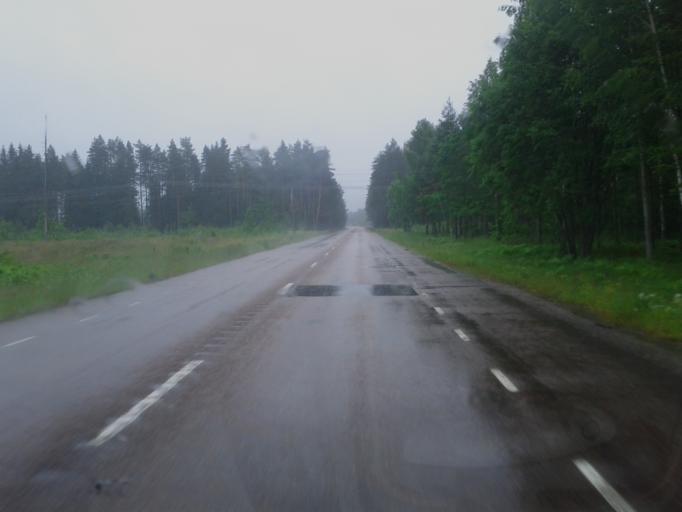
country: SE
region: Uppsala
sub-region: Alvkarleby Kommun
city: AElvkarleby
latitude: 60.5558
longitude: 17.4516
